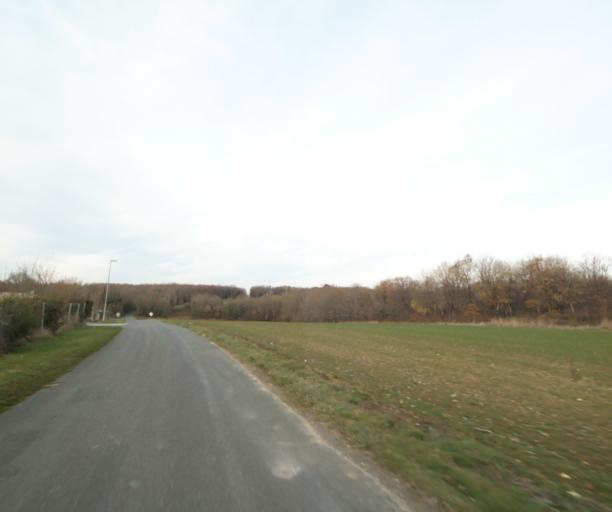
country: FR
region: Poitou-Charentes
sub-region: Departement de la Charente-Maritime
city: Fontcouverte
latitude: 45.8107
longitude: -0.5783
